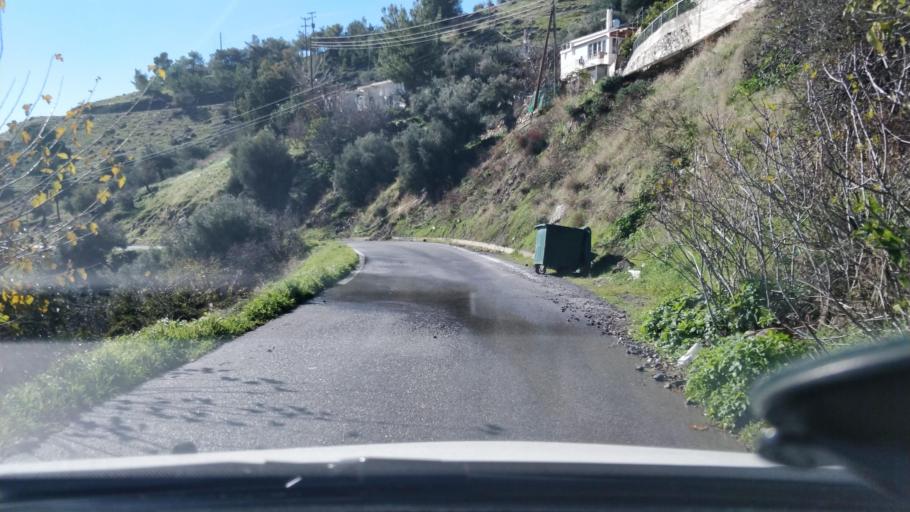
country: GR
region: Crete
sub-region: Nomos Irakleiou
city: Kastelli
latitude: 35.0399
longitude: 25.4446
